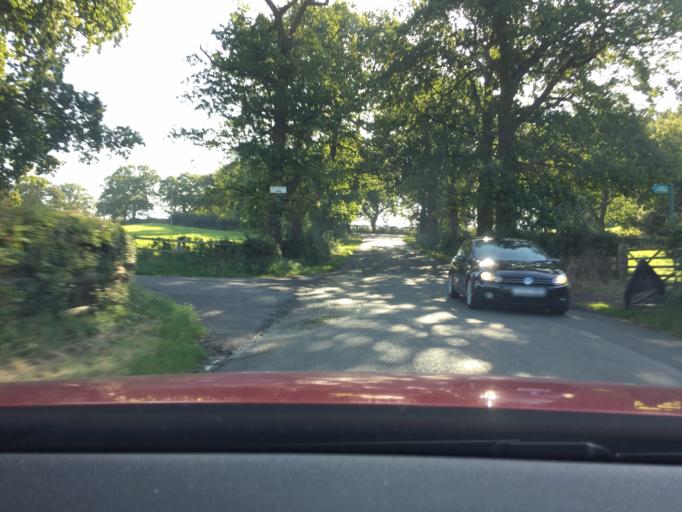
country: GB
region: England
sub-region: Leicestershire
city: Houghton on the Hill
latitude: 52.6359
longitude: -0.9536
